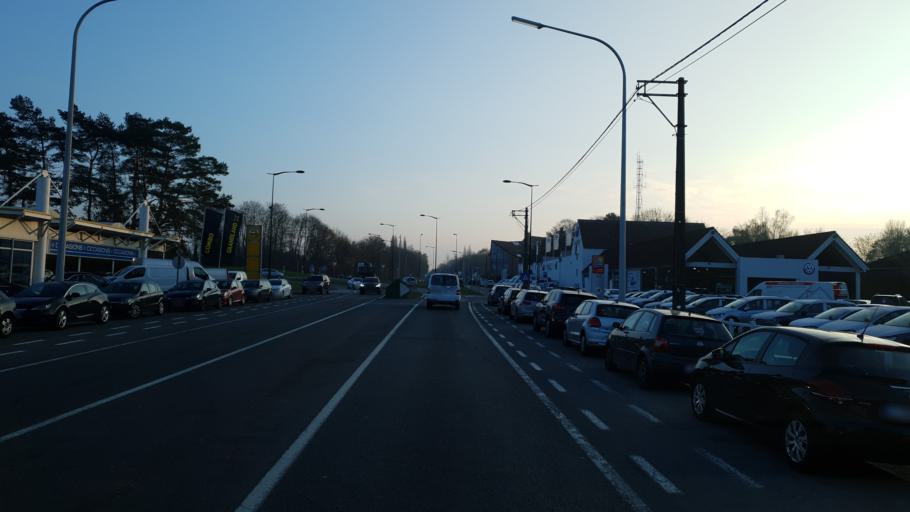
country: BE
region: Wallonia
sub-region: Province du Brabant Wallon
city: Louvain-la-Neuve
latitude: 50.6916
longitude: 4.6156
